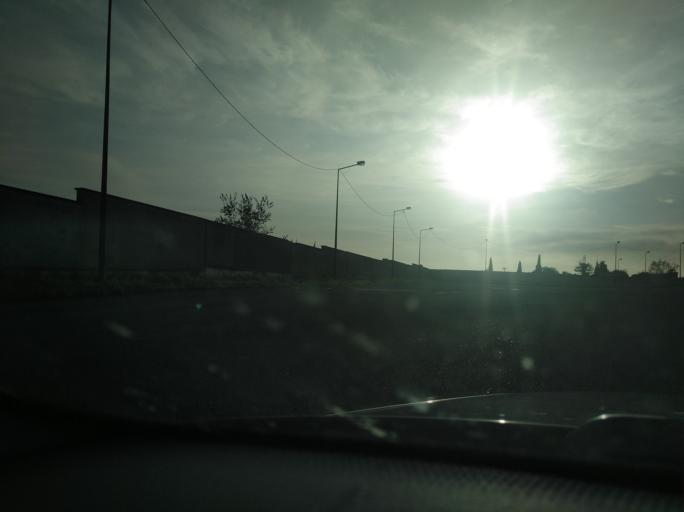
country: PT
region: Lisbon
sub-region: Odivelas
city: Odivelas
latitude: 38.7766
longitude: -9.1835
